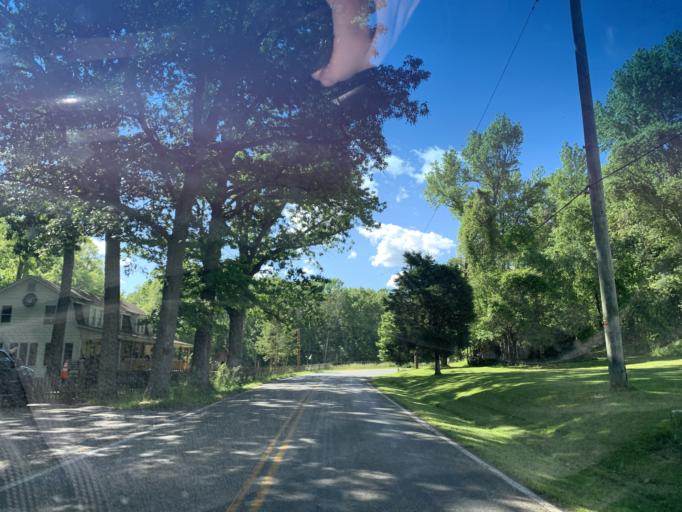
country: US
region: Maryland
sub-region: Cecil County
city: North East
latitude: 39.5421
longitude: -75.9169
